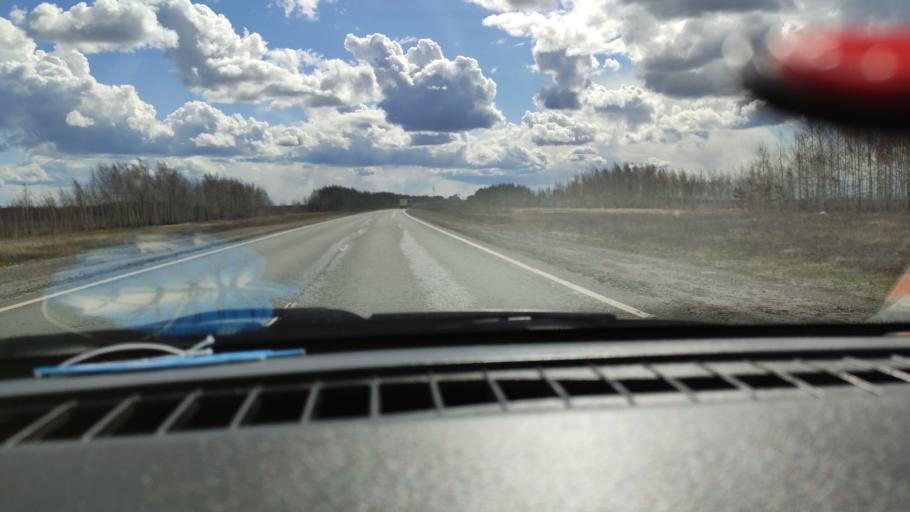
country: RU
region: Saratov
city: Dukhovnitskoye
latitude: 52.8468
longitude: 48.2534
